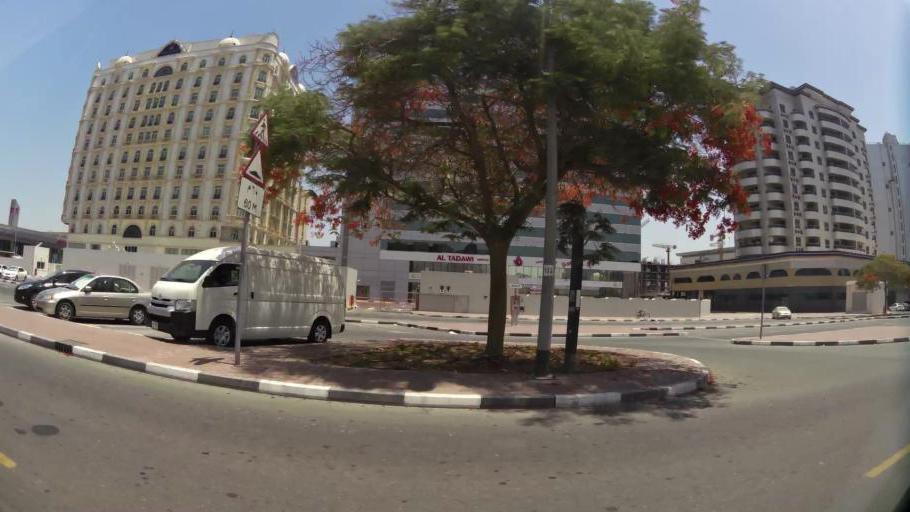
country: AE
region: Ash Shariqah
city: Sharjah
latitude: 25.2560
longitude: 55.3332
